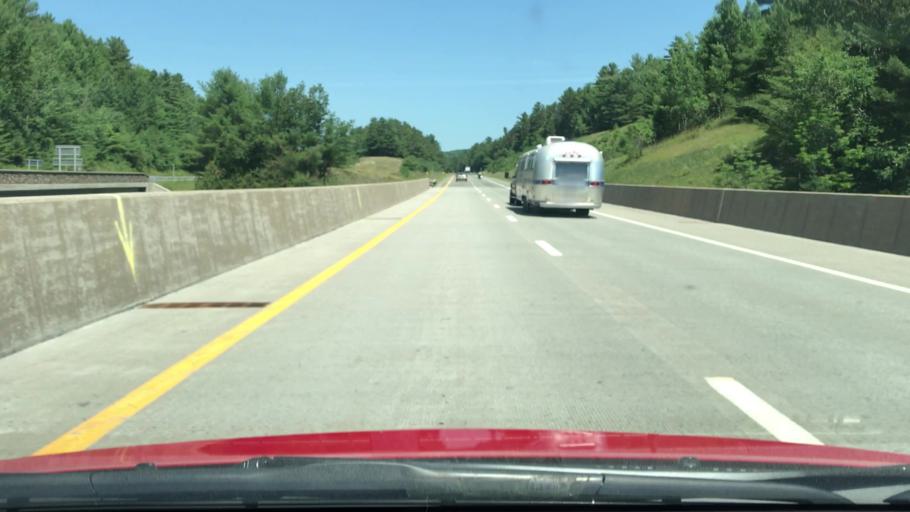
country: US
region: New York
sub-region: Essex County
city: Elizabethtown
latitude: 44.3082
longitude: -73.5296
